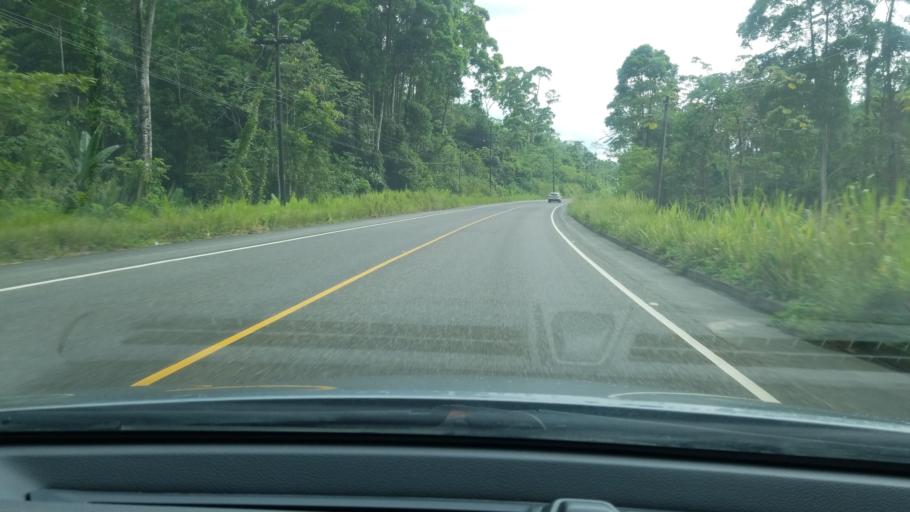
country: HN
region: Cortes
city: Potrerillos
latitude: 15.6067
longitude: -88.2916
